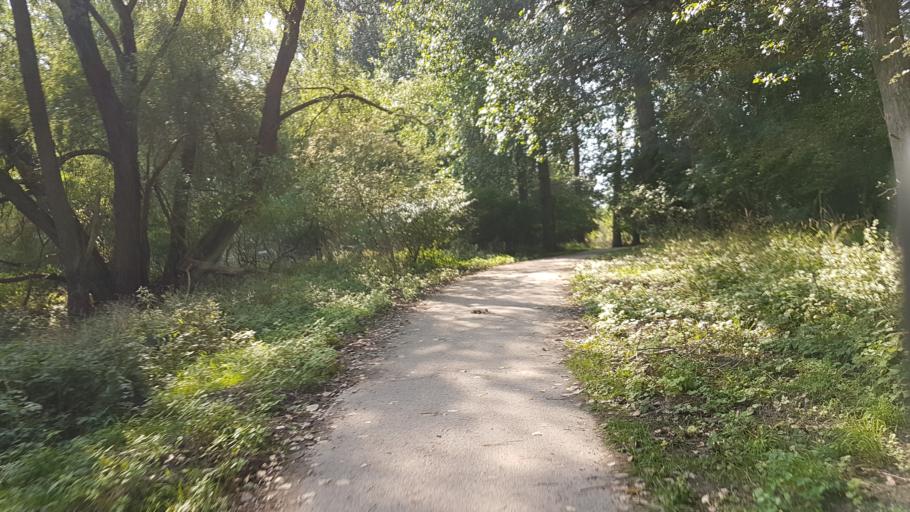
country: DE
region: Mecklenburg-Vorpommern
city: Glowe
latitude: 54.5619
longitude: 13.4881
